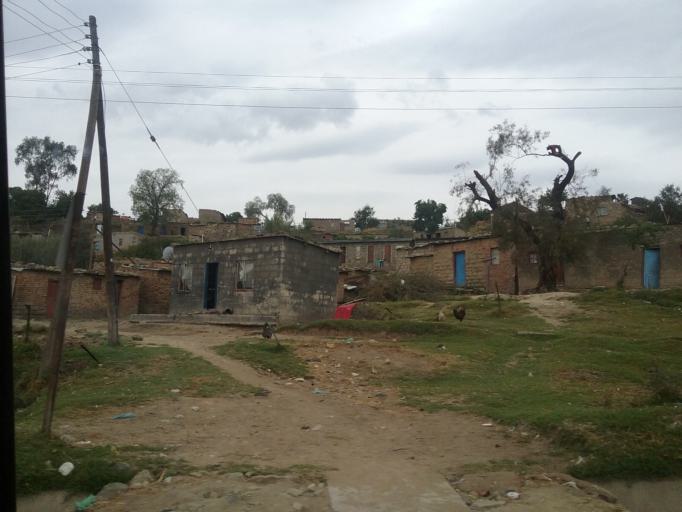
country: LS
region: Maseru
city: Maseru
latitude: -29.3229
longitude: 27.5090
